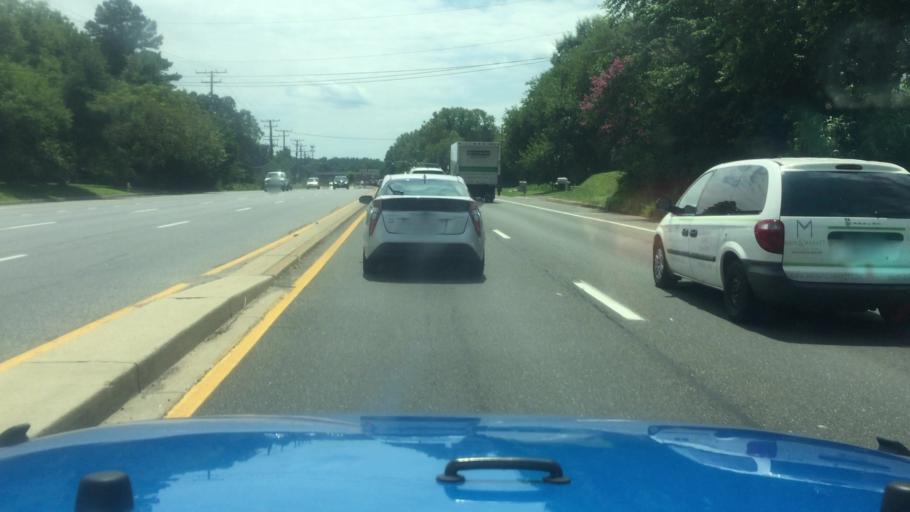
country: US
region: Maryland
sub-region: Anne Arundel County
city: Edgewater
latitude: 38.9655
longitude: -76.5456
